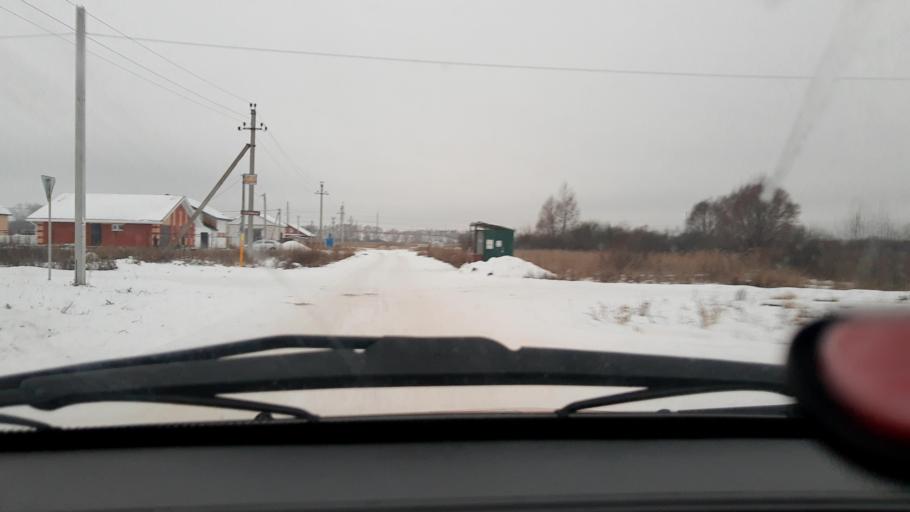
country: RU
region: Bashkortostan
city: Mikhaylovka
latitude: 54.7907
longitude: 55.8227
